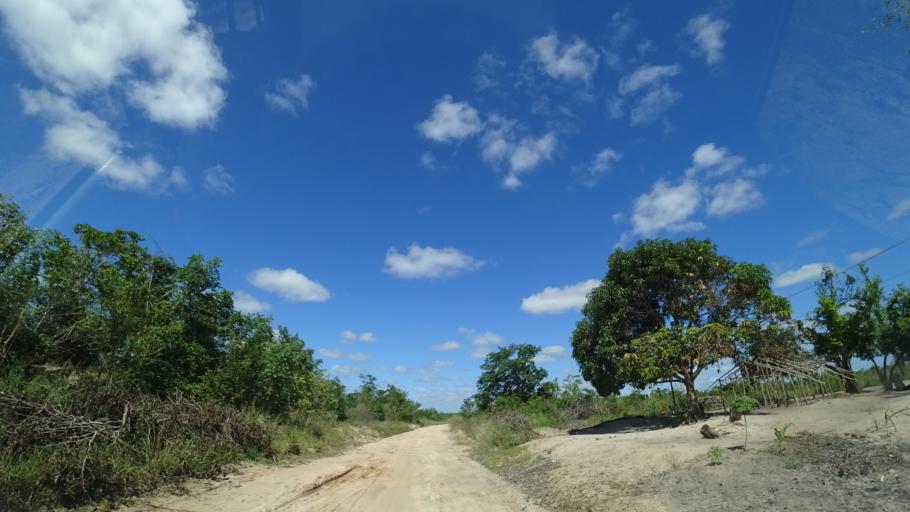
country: MZ
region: Sofala
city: Dondo
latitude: -19.2941
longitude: 34.6903
